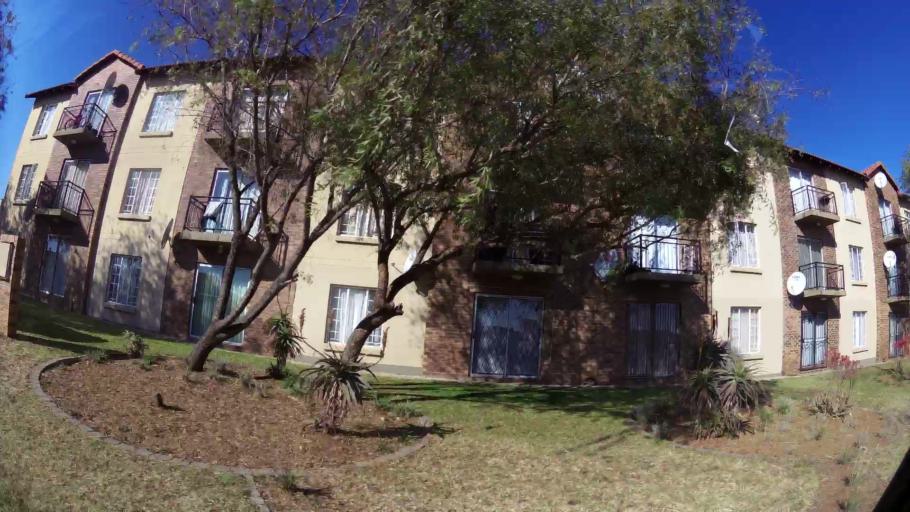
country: ZA
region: Gauteng
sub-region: City of Johannesburg Metropolitan Municipality
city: Midrand
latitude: -25.9195
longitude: 28.1311
